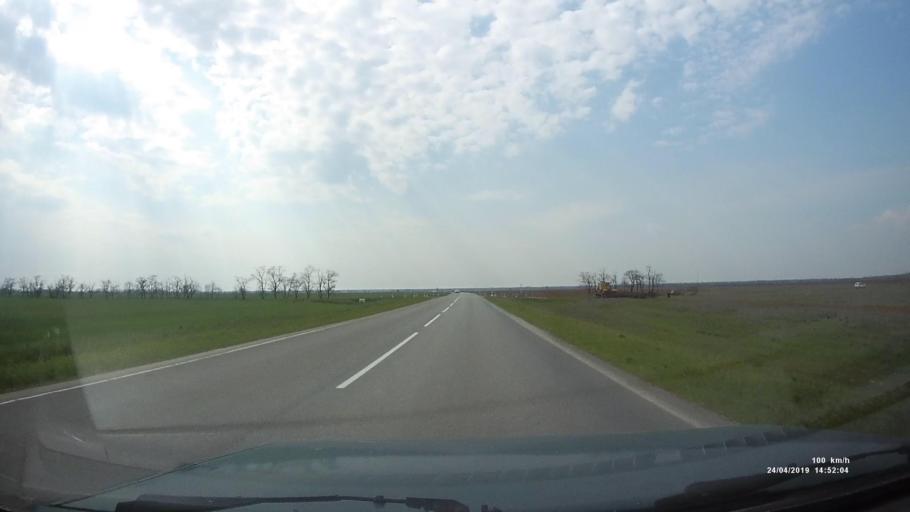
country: RU
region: Rostov
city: Remontnoye
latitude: 46.5292
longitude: 43.6883
